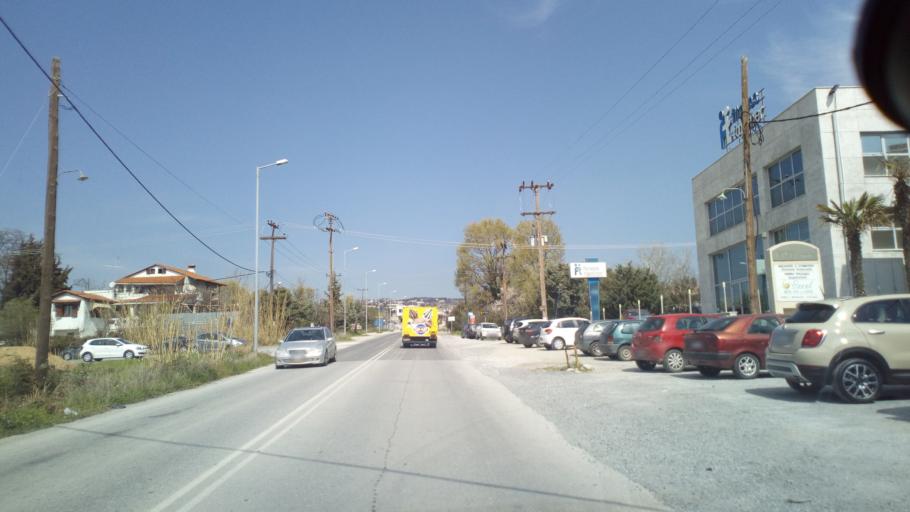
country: GR
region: Central Macedonia
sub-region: Nomos Thessalonikis
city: Thermi
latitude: 40.5543
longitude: 23.0187
